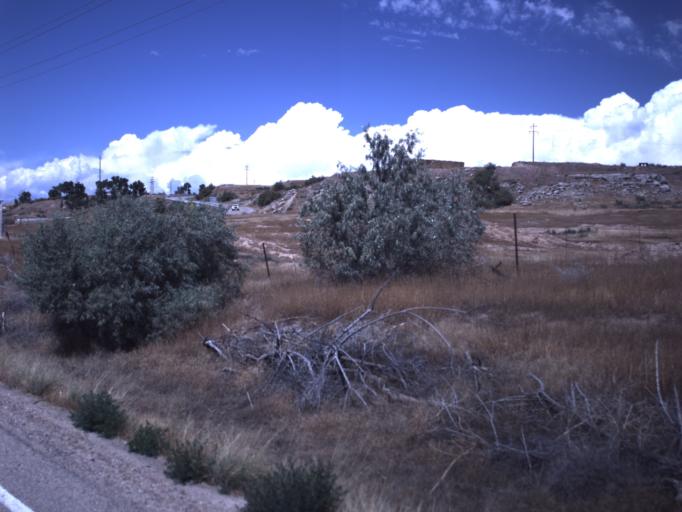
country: US
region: Utah
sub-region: Uintah County
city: Maeser
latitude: 40.2190
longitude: -109.6818
